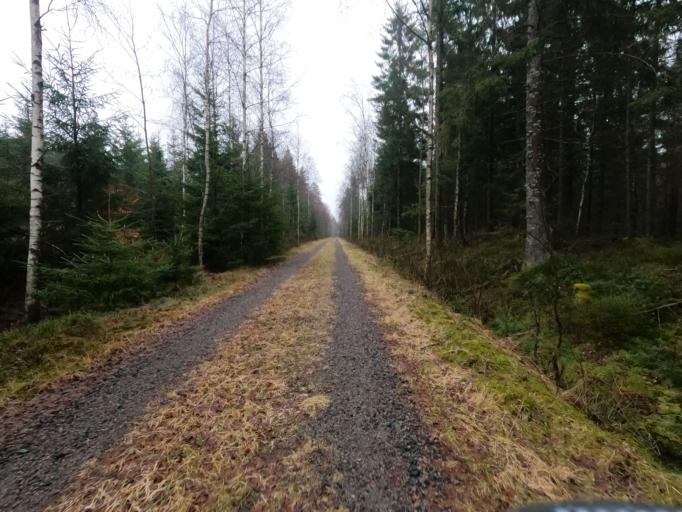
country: SE
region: Halland
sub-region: Hylte Kommun
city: Hyltebruk
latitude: 56.8182
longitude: 13.3088
